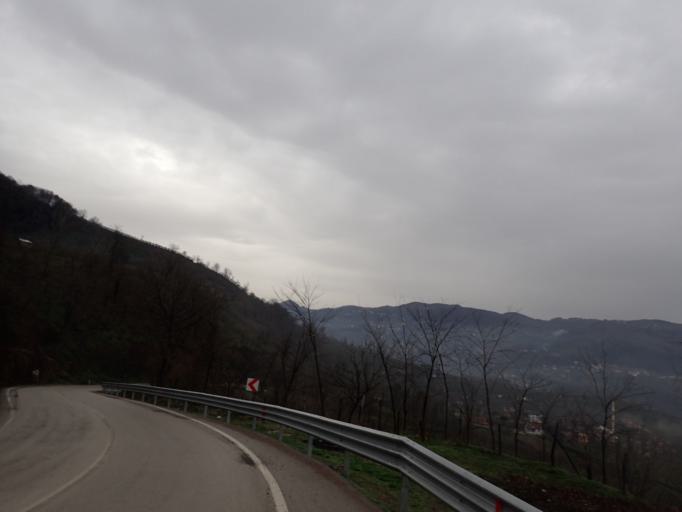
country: TR
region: Ordu
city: Camas
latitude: 40.9293
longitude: 37.5071
